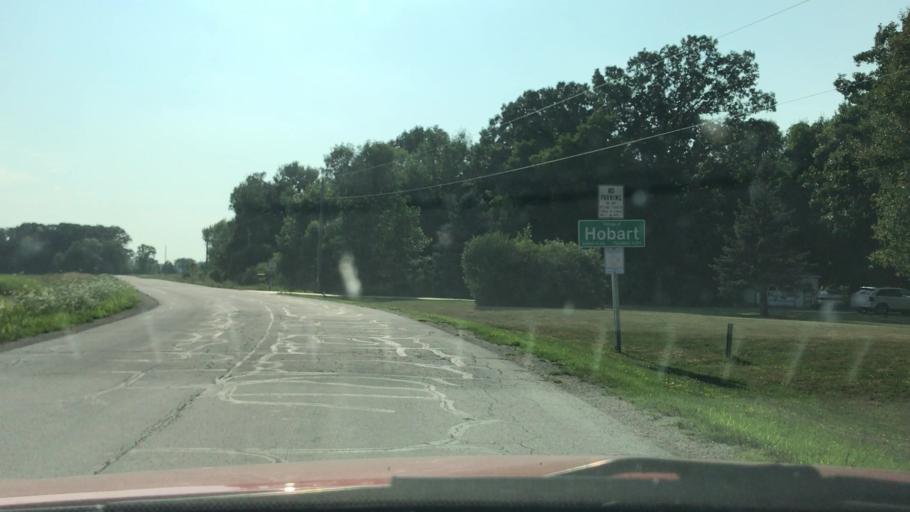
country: US
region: Wisconsin
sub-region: Brown County
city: Oneida
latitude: 44.4311
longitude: -88.1505
